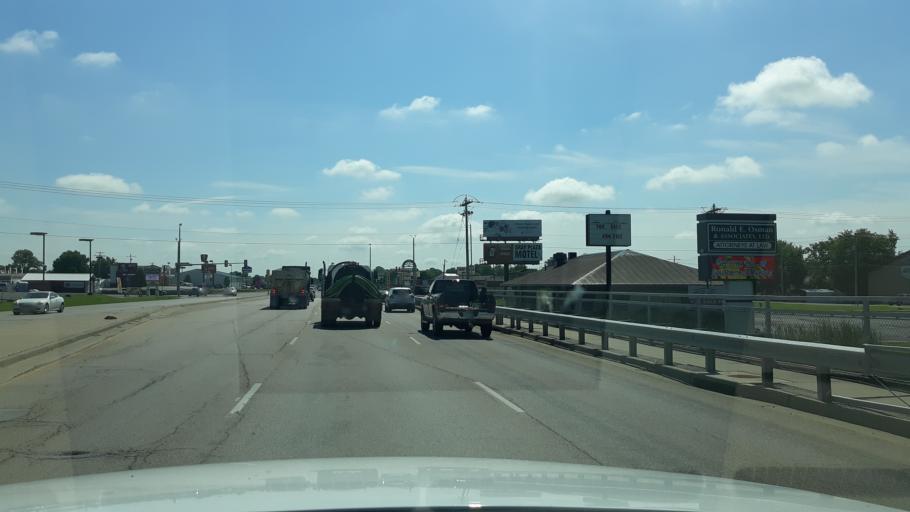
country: US
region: Illinois
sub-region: Williamson County
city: Marion
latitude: 37.7406
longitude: -88.9441
